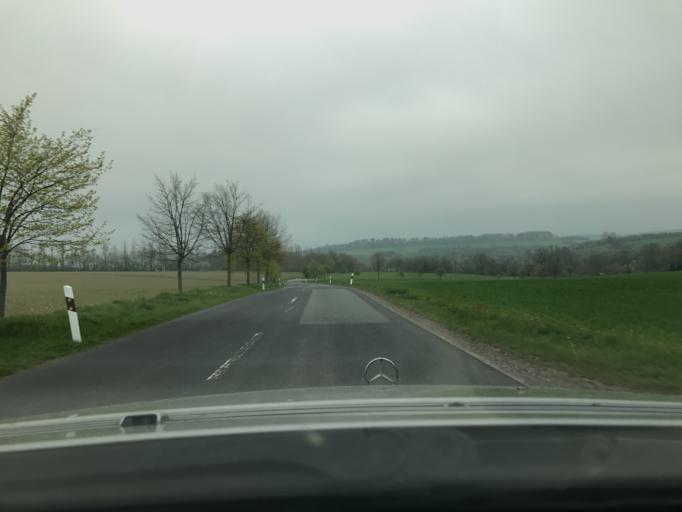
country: DE
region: Thuringia
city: Kreuzebra
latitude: 51.3356
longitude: 10.2643
